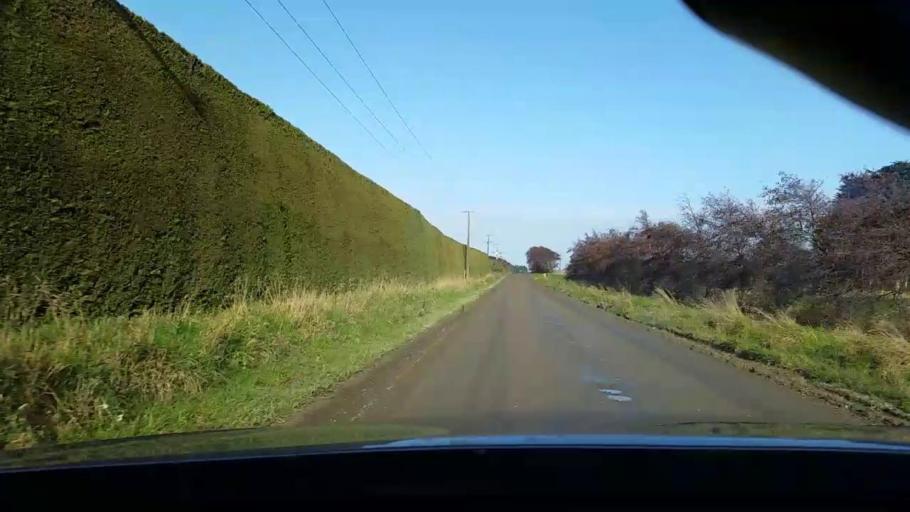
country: NZ
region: Southland
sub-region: Invercargill City
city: Invercargill
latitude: -46.3009
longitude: 168.3033
